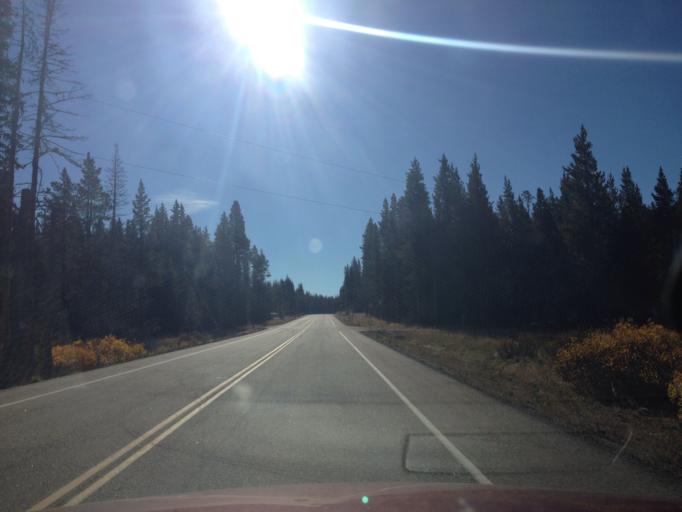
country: US
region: Montana
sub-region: Carbon County
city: Red Lodge
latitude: 45.0248
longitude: -109.8815
